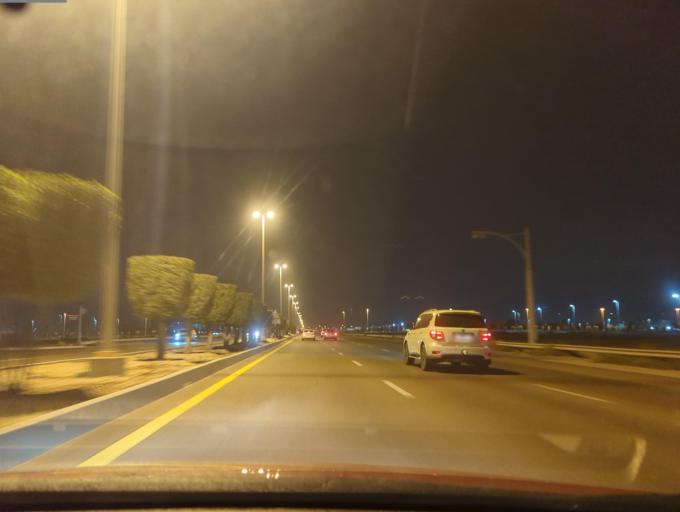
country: AE
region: Abu Dhabi
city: Abu Dhabi
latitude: 24.3884
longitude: 54.7191
